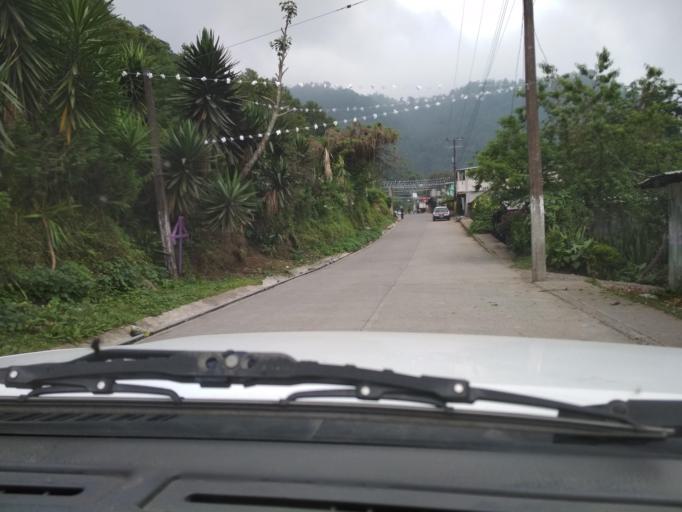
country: MX
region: Veracruz
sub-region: La Perla
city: Metlac Hernandez (Metlac Primero)
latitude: 18.9773
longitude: -97.1413
